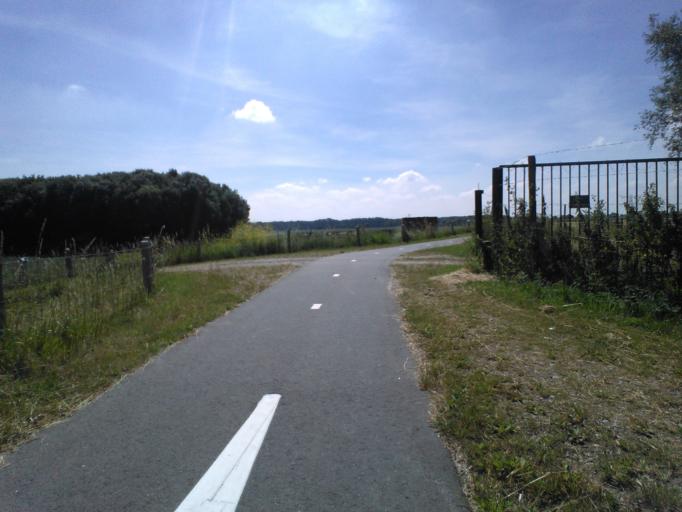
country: NL
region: North Brabant
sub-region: Gemeente Werkendam
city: Werkendam
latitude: 51.7658
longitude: 4.8640
